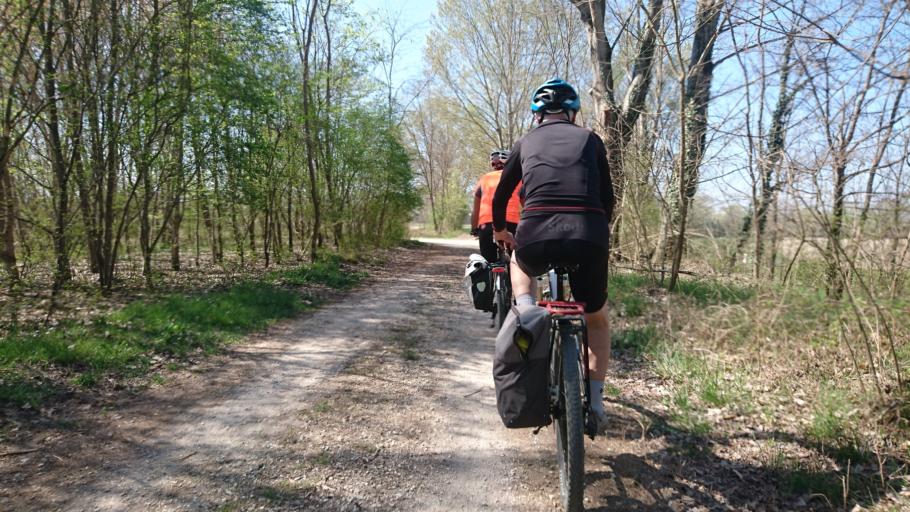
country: IT
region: Veneto
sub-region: Provincia di Padova
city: Piazzola sul Brenta
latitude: 45.5714
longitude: 11.7596
